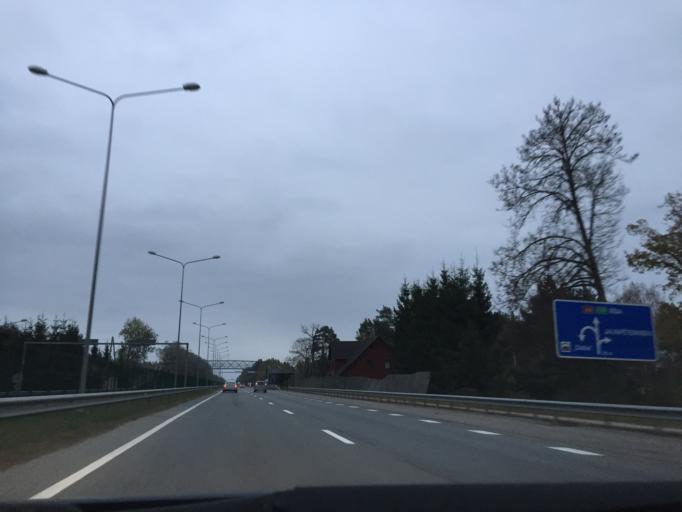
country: LV
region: Olaine
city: Olaine
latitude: 56.7413
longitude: 23.8777
